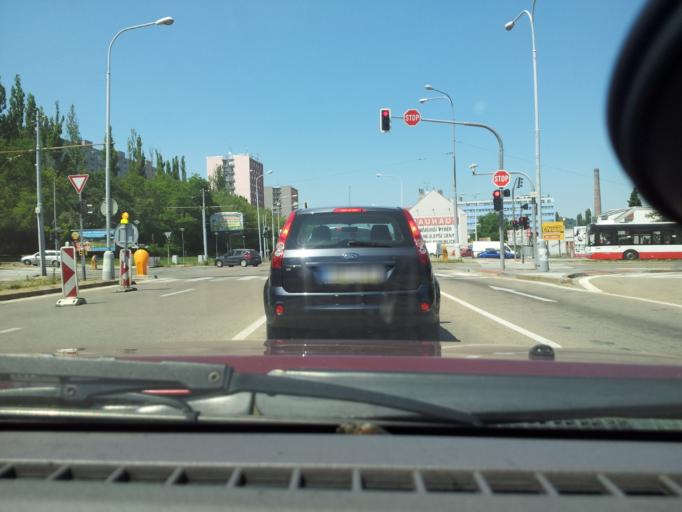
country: CZ
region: South Moravian
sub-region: Mesto Brno
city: Brno
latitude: 49.1722
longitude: 16.5973
